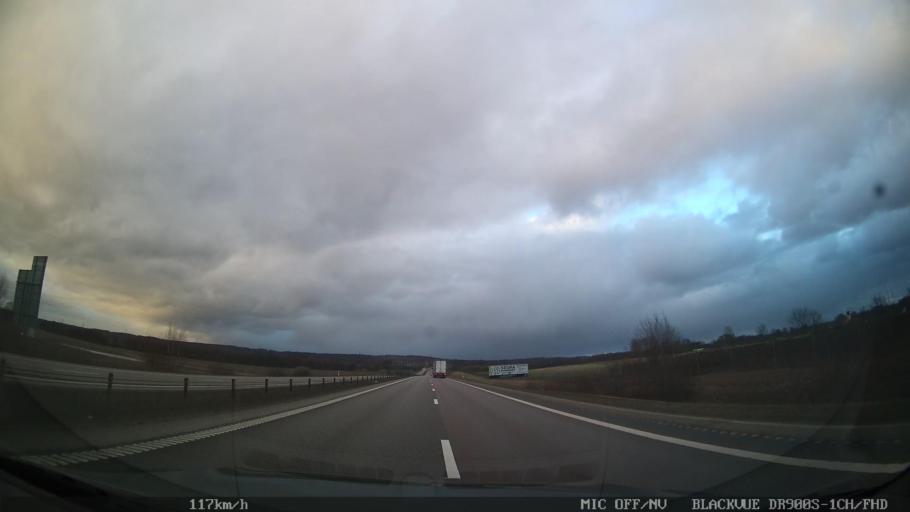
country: SE
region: Skane
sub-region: Astorps Kommun
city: Kvidinge
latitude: 56.1952
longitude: 13.0671
